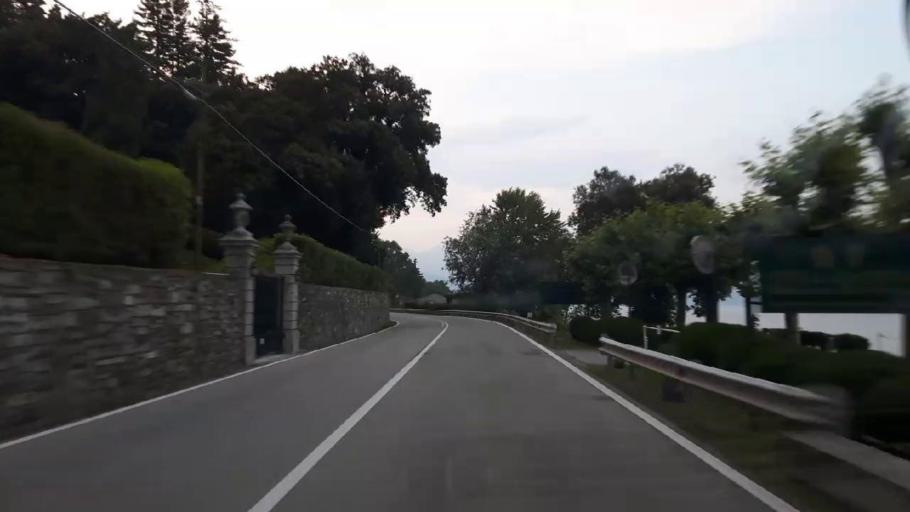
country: IT
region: Piedmont
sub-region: Provincia Verbano-Cusio-Ossola
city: Belgirate
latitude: 45.8485
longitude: 8.5710
